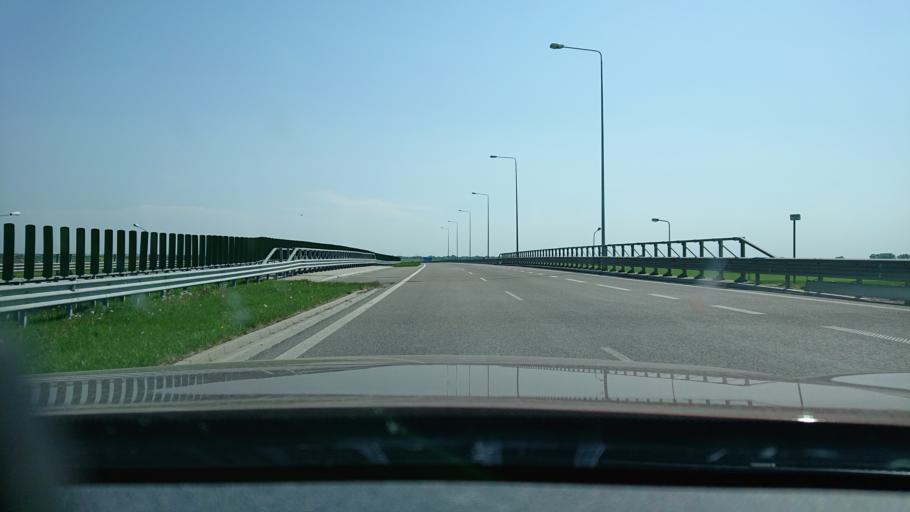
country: PL
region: Subcarpathian Voivodeship
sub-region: Powiat jaroslawski
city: Radymno
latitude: 49.9104
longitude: 22.8174
